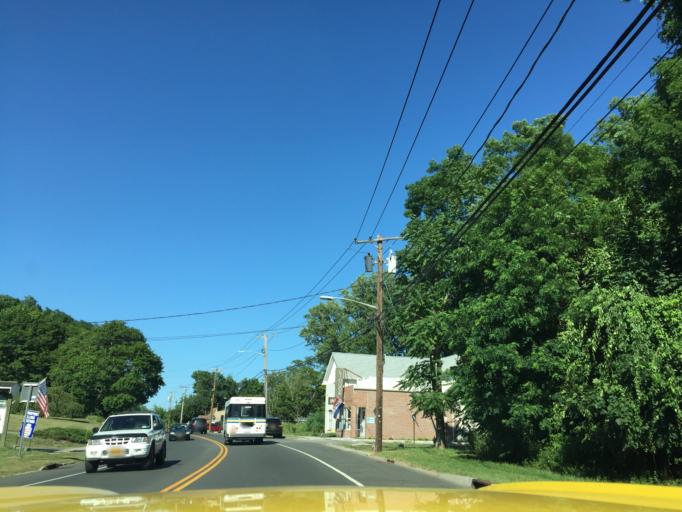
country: US
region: New York
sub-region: Suffolk County
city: Jamesport
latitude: 40.9481
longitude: -72.5843
